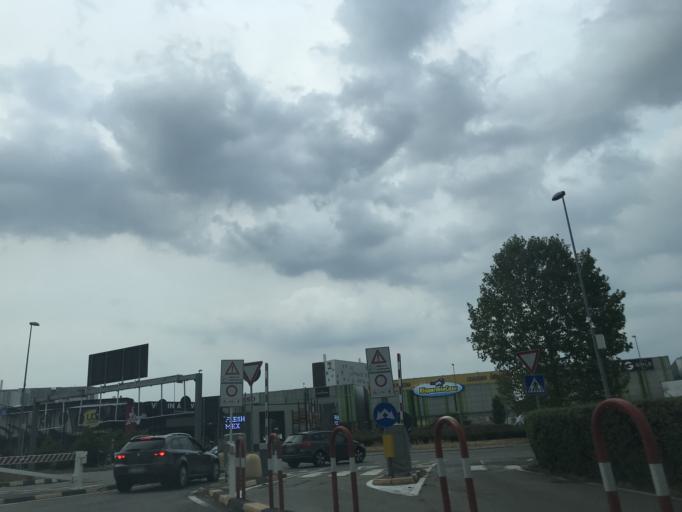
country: IT
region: Lombardy
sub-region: Citta metropolitana di Milano
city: Rozzano
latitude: 45.4051
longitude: 9.1515
